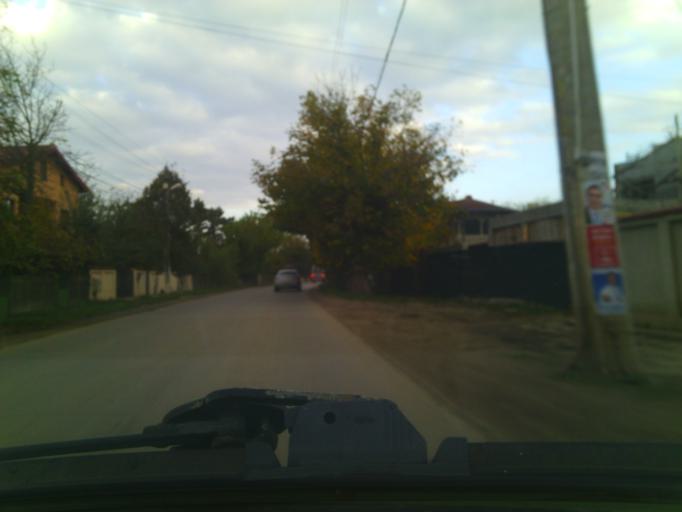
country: RO
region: Ilfov
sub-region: Comuna Berceni
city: Berceni
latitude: 44.3183
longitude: 26.1820
